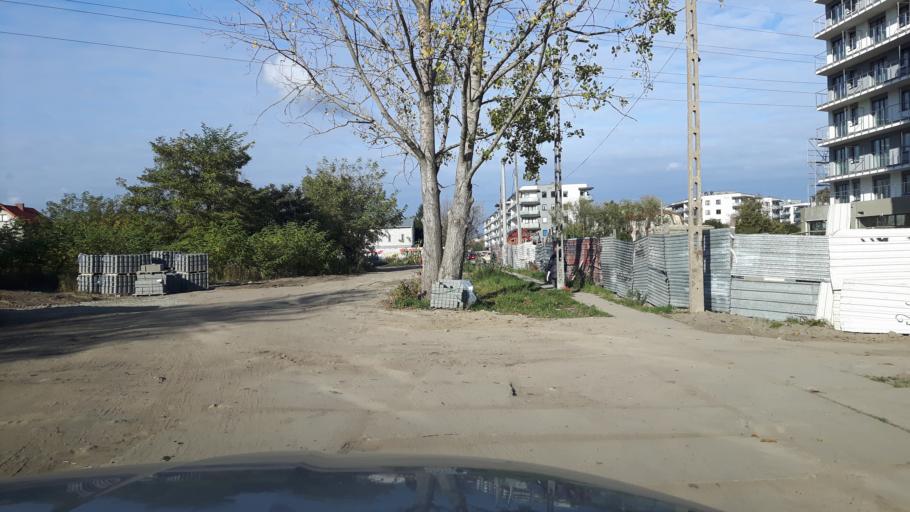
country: PL
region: Masovian Voivodeship
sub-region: Powiat wolominski
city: Zabki
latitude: 52.2805
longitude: 21.1216
